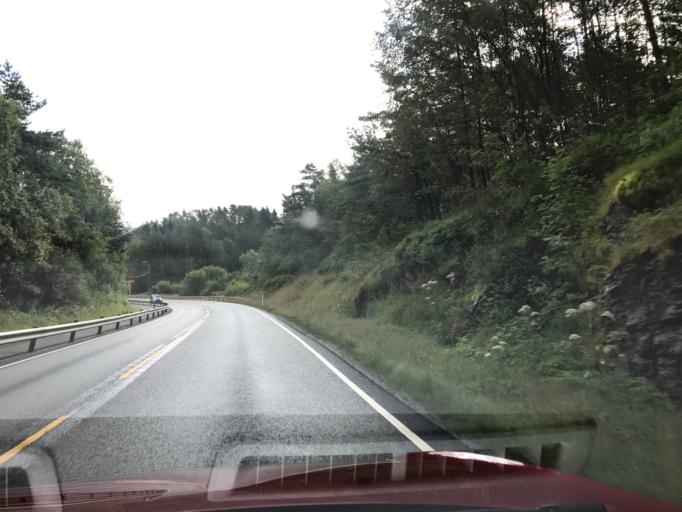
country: NO
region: Hordaland
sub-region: Sveio
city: Sveio
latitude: 59.5804
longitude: 5.4320
